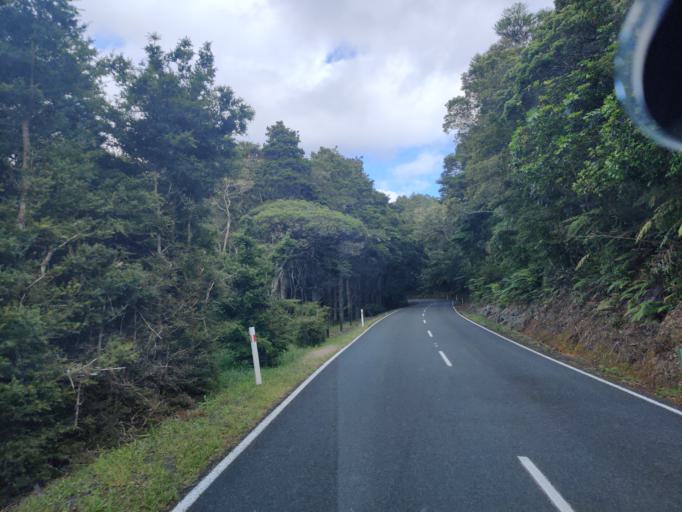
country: NZ
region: Northland
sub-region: Whangarei
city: Ngunguru
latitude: -35.5787
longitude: 174.4152
